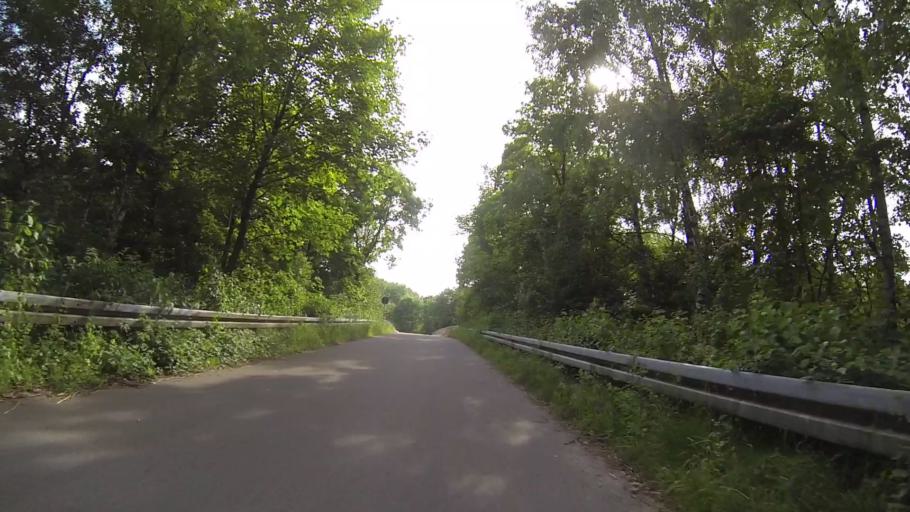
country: DE
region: Bavaria
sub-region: Swabia
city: Neu-Ulm
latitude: 48.3647
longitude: 10.0030
